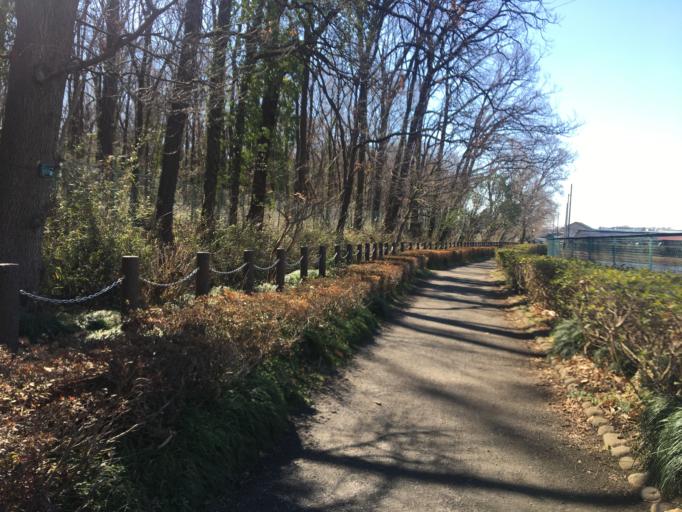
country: JP
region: Saitama
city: Asaka
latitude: 35.7915
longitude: 139.5563
